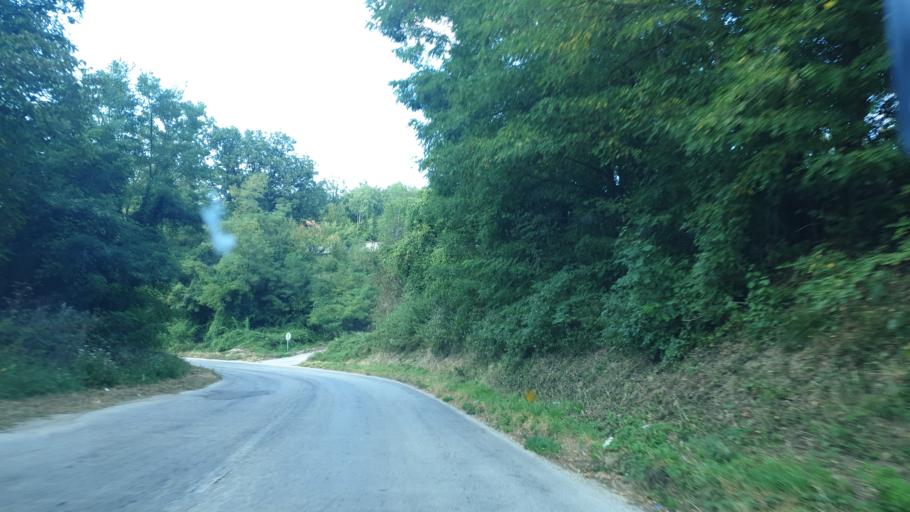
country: RS
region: Central Serbia
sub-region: Zlatiborski Okrug
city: Uzice
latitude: 43.8619
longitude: 19.9080
